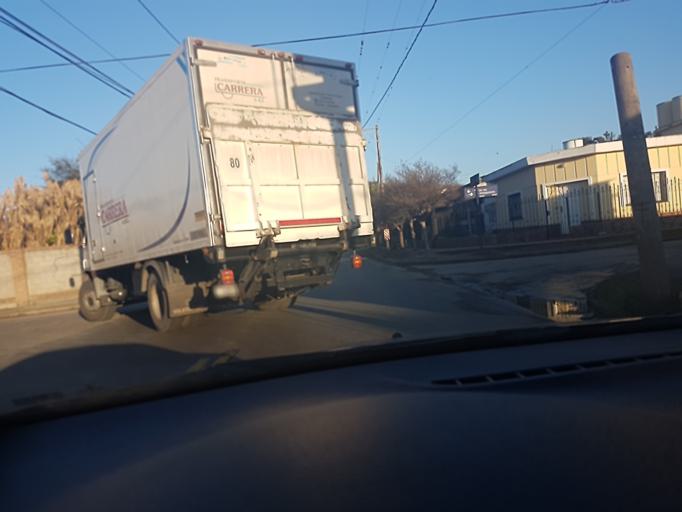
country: AR
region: Cordoba
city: Villa Allende
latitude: -31.3433
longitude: -64.2280
